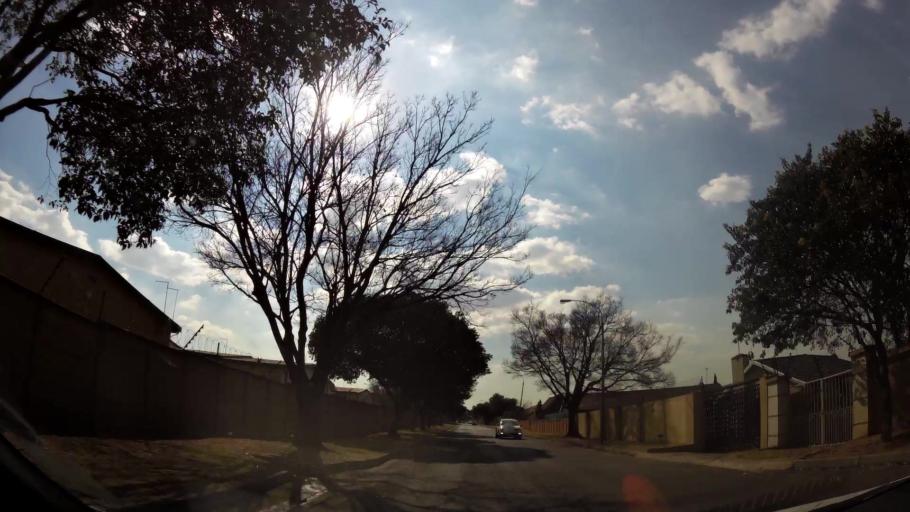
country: ZA
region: Gauteng
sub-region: Ekurhuleni Metropolitan Municipality
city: Germiston
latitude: -26.1827
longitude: 28.2030
